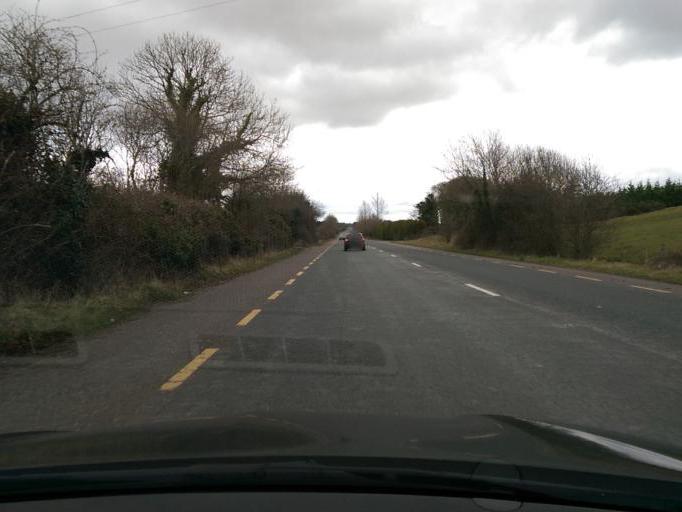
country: IE
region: Leinster
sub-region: Uibh Fhaili
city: Clara
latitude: 53.3979
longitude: -7.6423
